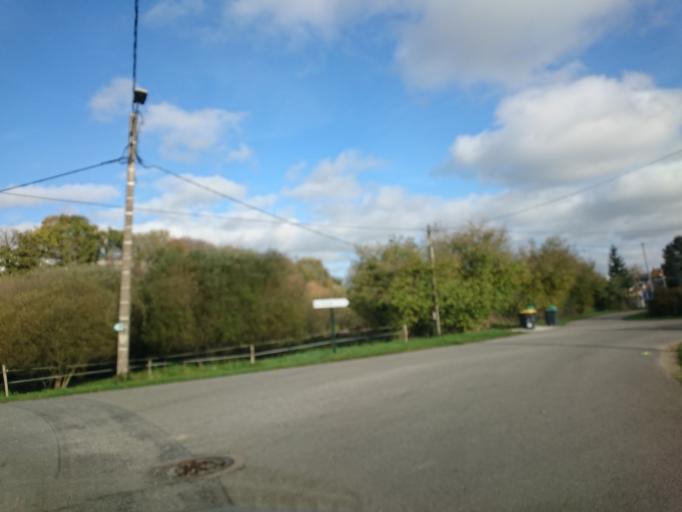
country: FR
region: Brittany
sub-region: Departement d'Ille-et-Vilaine
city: Bain-de-Bretagne
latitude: 47.8451
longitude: -1.6753
